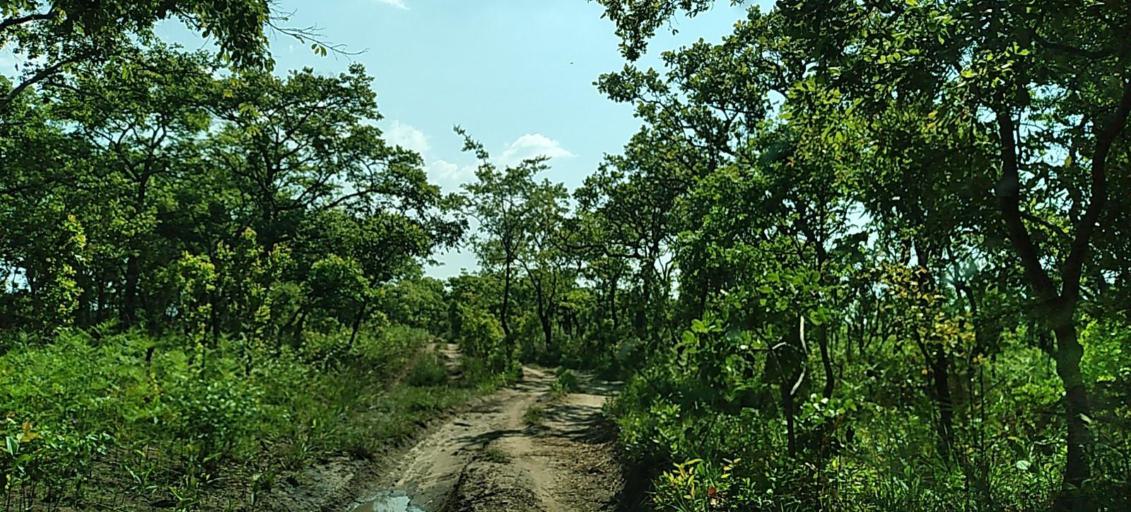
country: CD
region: Katanga
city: Kolwezi
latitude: -11.2620
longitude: 25.0058
